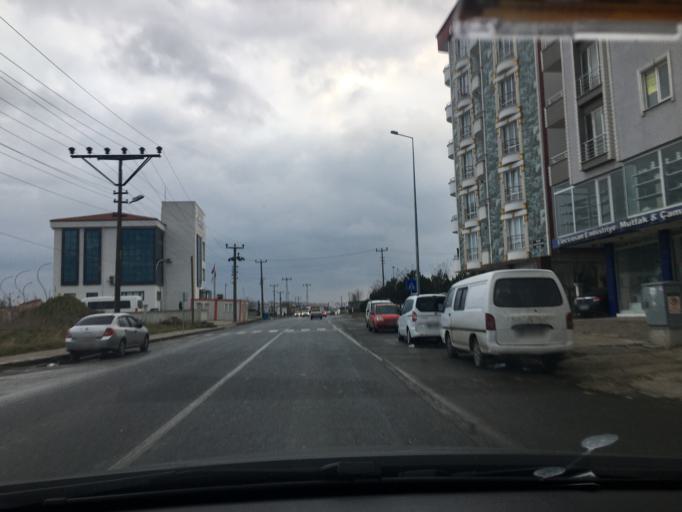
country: TR
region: Tekirdag
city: Cerkezkoey
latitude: 41.2795
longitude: 27.9893
